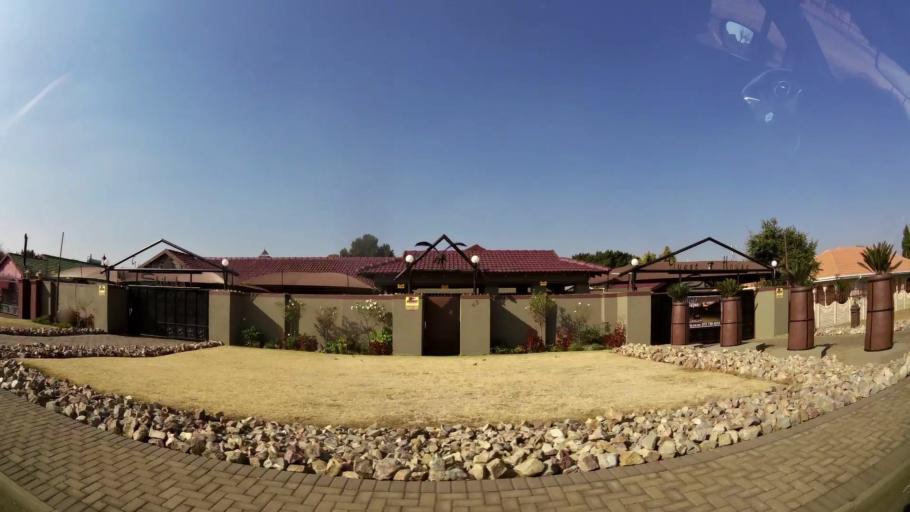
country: ZA
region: Gauteng
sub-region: West Rand District Municipality
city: Randfontein
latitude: -26.1813
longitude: 27.6803
